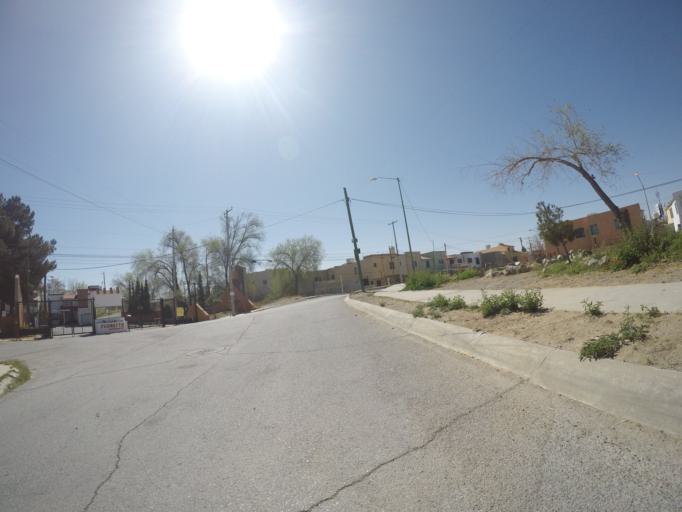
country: MX
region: Chihuahua
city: Ciudad Juarez
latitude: 31.6903
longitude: -106.4155
